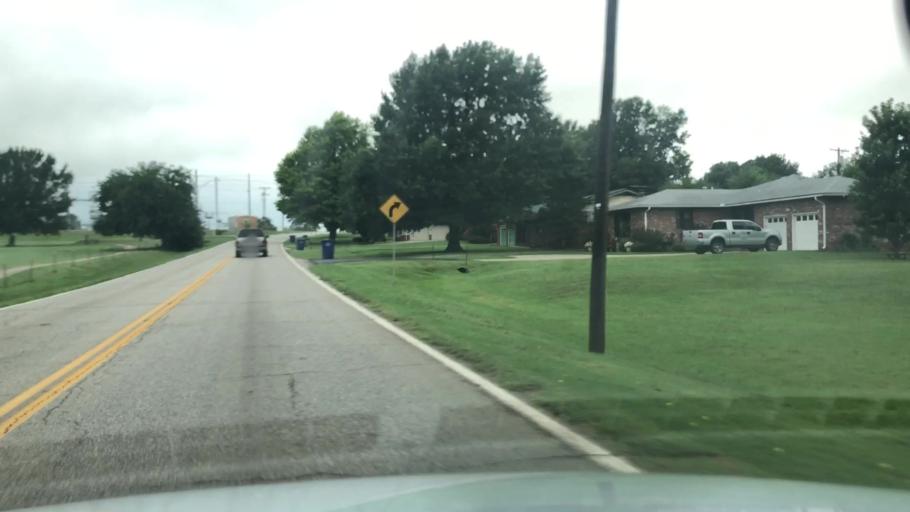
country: US
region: Oklahoma
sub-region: Nowata County
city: Nowata
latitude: 36.7027
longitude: -95.6458
